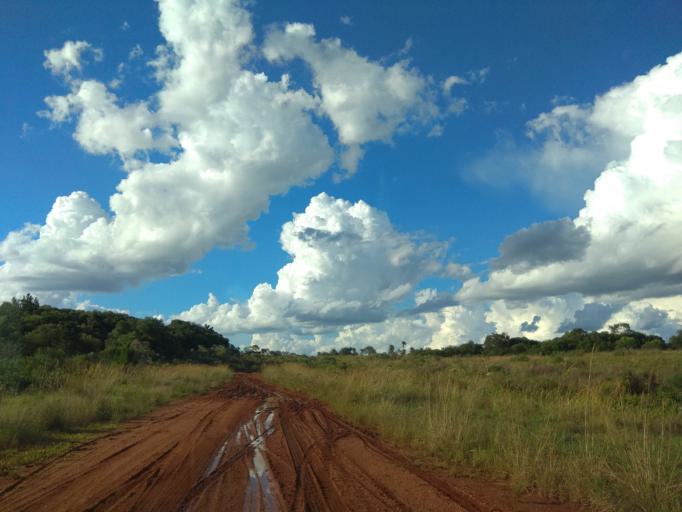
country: AR
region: Misiones
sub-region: Departamento de Candelaria
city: Candelaria
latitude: -27.4906
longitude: -55.7584
